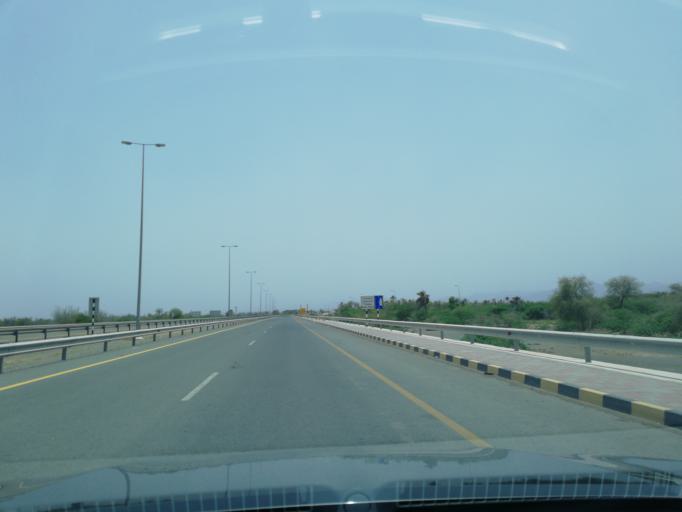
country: OM
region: Al Batinah
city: Shinas
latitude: 24.7426
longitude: 56.4586
